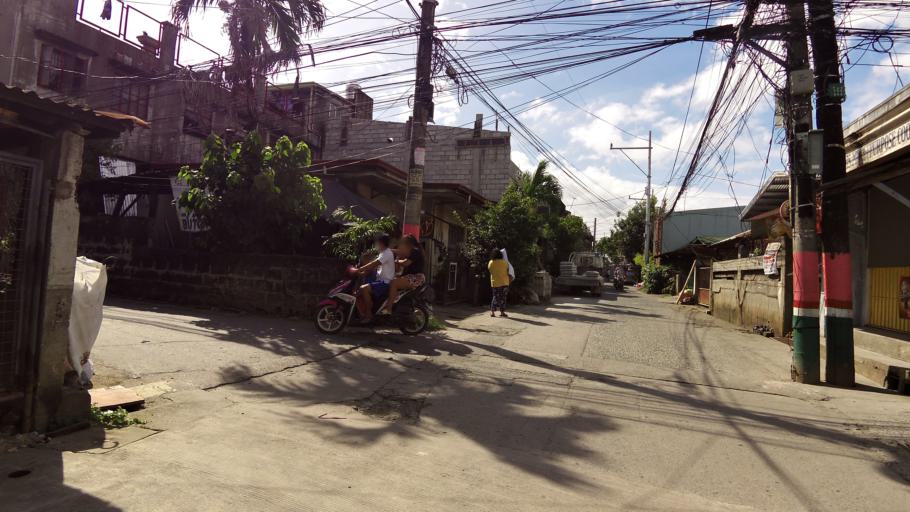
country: PH
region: Calabarzon
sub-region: Province of Rizal
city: Cainta
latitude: 14.5704
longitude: 121.1284
